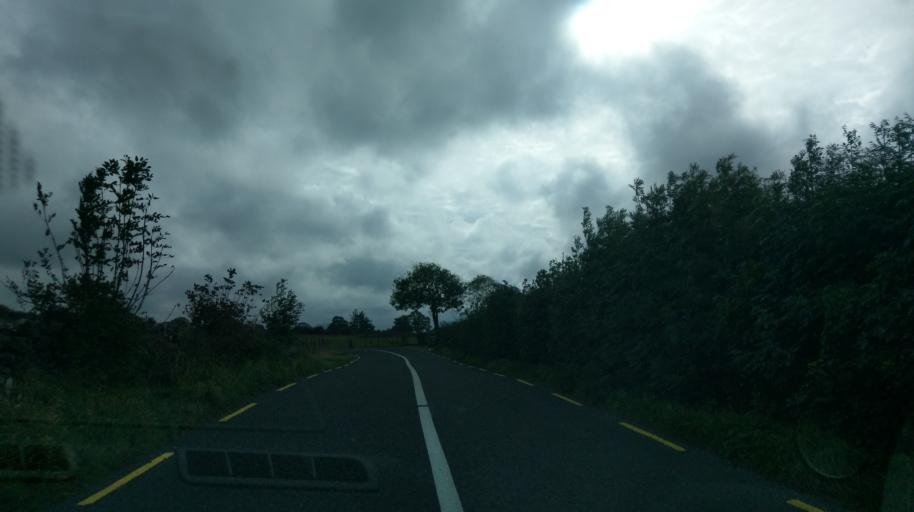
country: IE
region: Connaught
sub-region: County Galway
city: Ballinasloe
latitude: 53.4367
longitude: -8.4524
